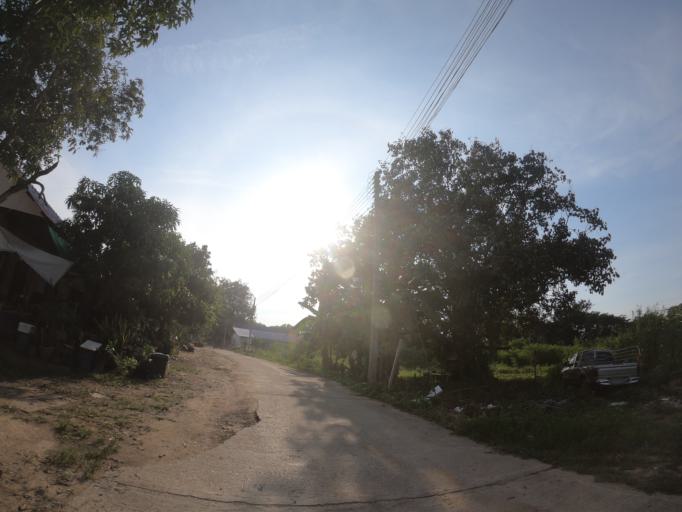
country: TH
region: Chiang Mai
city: Saraphi
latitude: 18.7220
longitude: 98.9842
